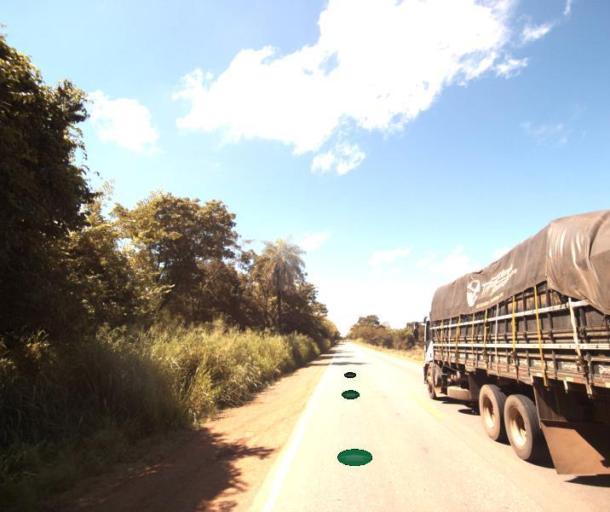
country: BR
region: Goias
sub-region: Jaragua
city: Jaragua
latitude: -15.6771
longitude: -49.3447
